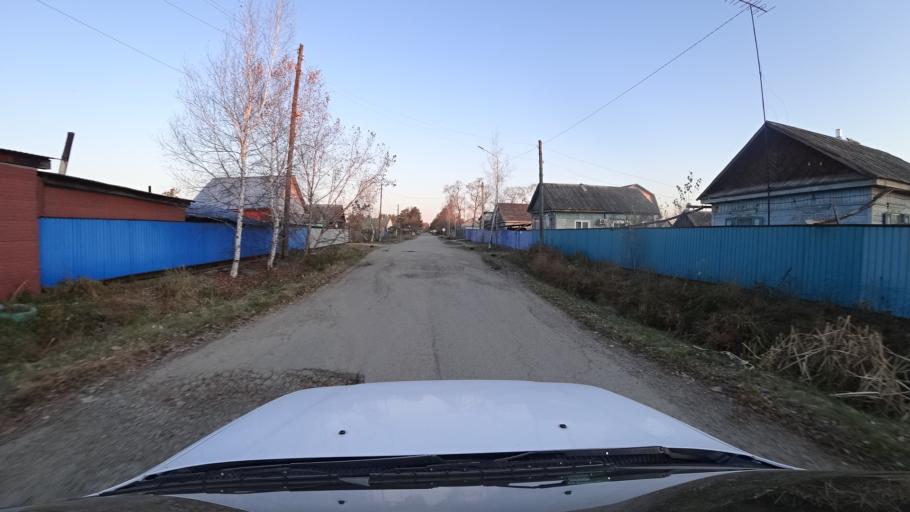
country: RU
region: Primorskiy
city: Dal'nerechensk
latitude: 45.9229
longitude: 133.7370
